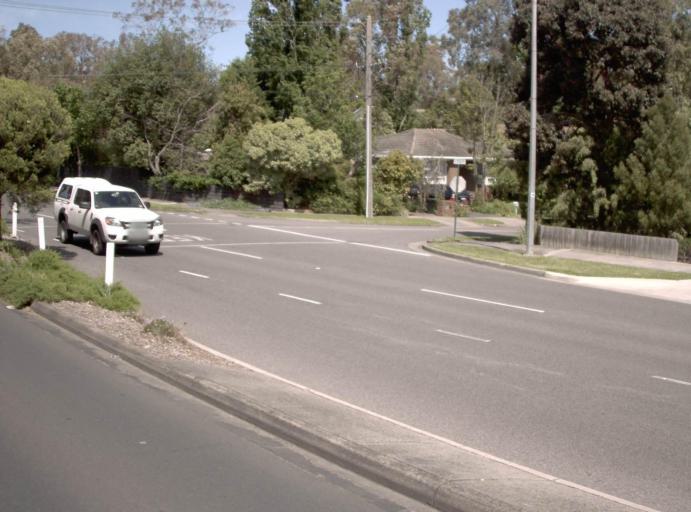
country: AU
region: Victoria
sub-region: Whitehorse
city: Blackburn South
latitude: -37.8335
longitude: 145.1567
